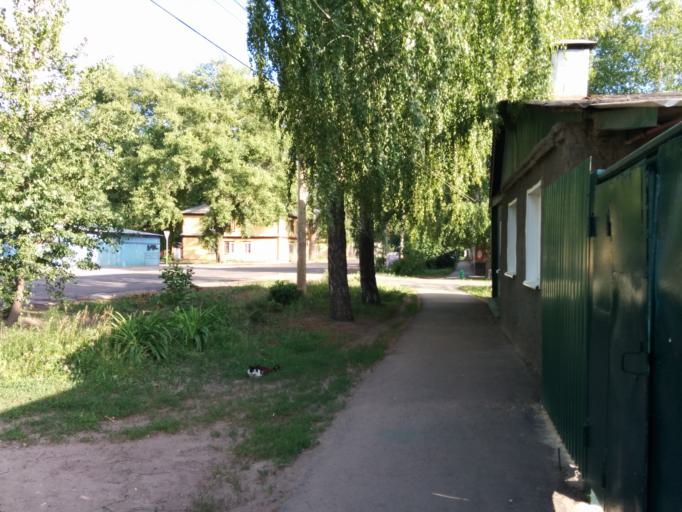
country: RU
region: Tambov
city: Tambov
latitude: 52.7515
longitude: 41.4402
